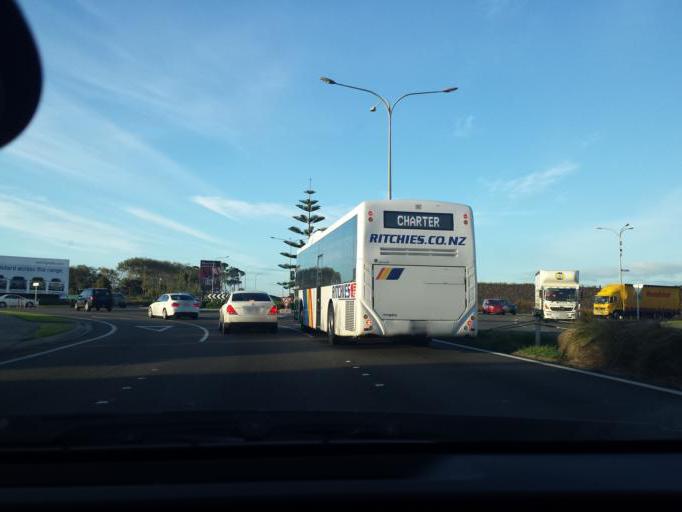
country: NZ
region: Auckland
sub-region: Auckland
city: Mangere
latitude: -36.9903
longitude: 174.7861
